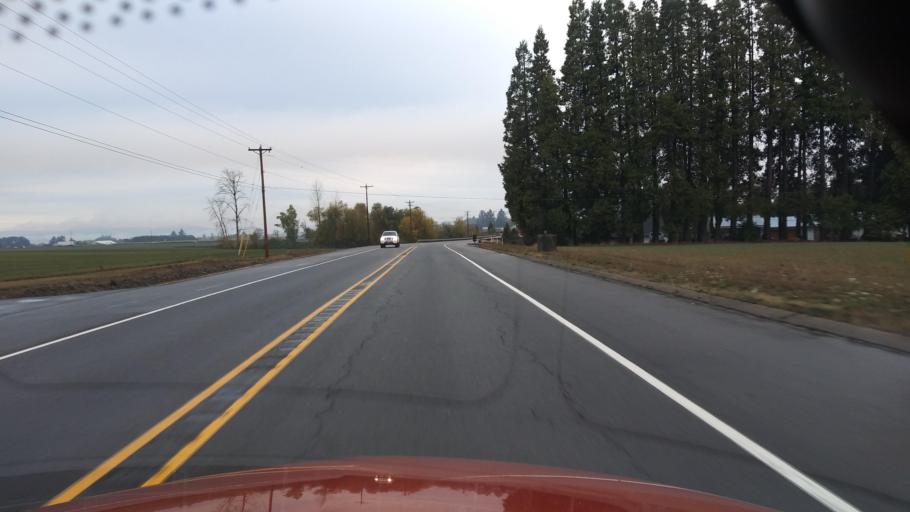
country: US
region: Oregon
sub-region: Washington County
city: Cornelius
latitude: 45.5476
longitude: -123.0608
